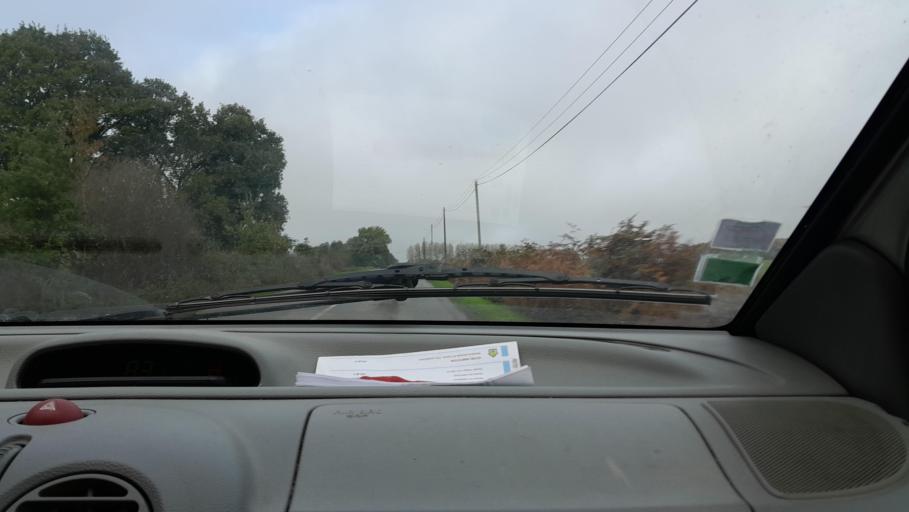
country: FR
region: Brittany
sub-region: Departement d'Ille-et-Vilaine
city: Luitre
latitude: 48.2280
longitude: -1.1006
